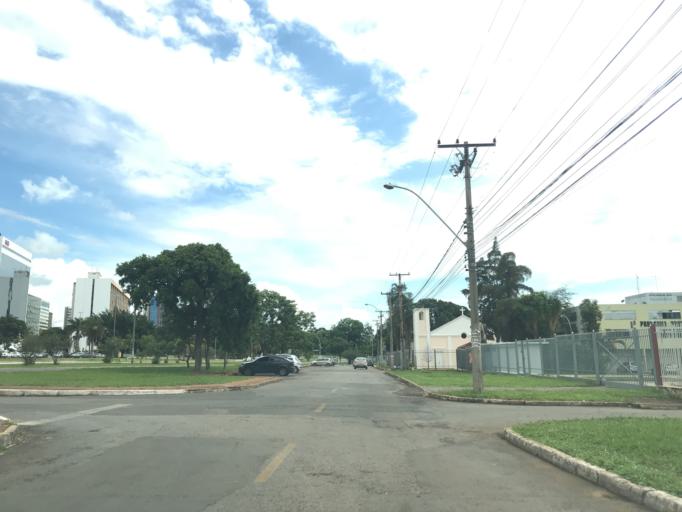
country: BR
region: Federal District
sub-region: Brasilia
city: Brasilia
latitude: -15.8068
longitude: -47.8807
